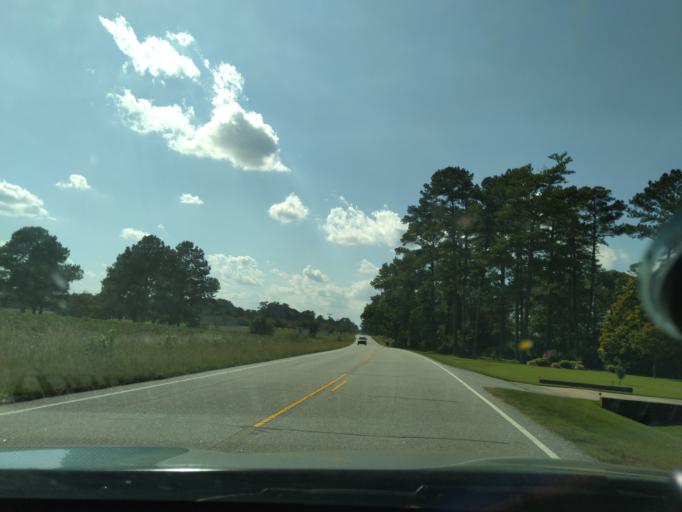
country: US
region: North Carolina
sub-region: Martin County
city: Robersonville
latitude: 35.8287
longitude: -77.2314
